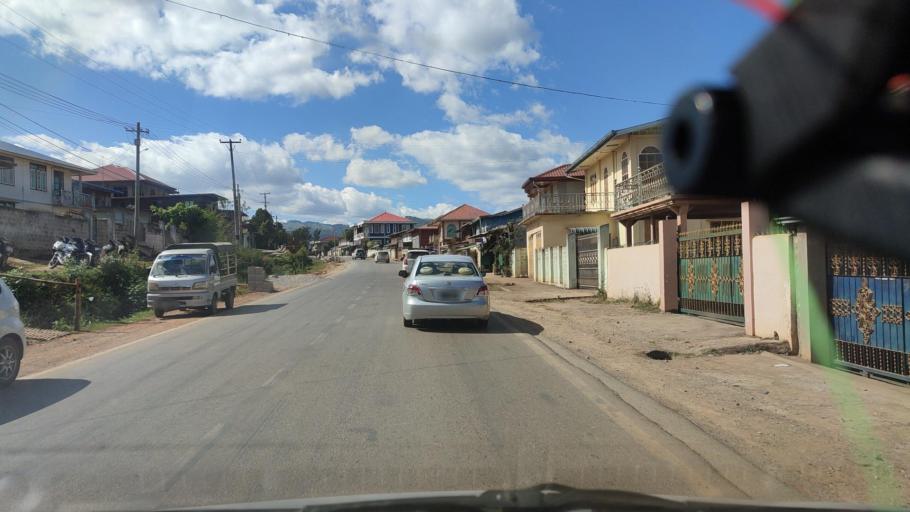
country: MM
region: Shan
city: Taunggyi
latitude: 20.9966
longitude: 97.5346
